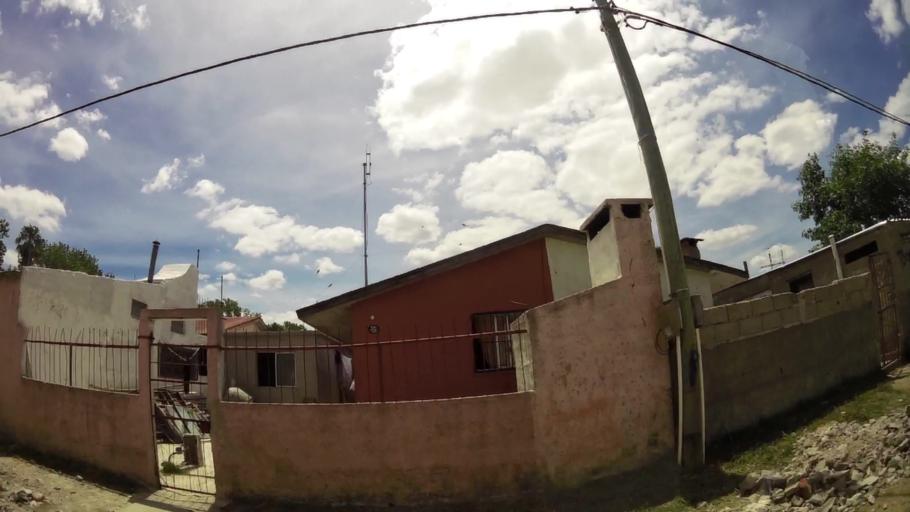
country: UY
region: Montevideo
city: Montevideo
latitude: -34.8604
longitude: -56.2511
